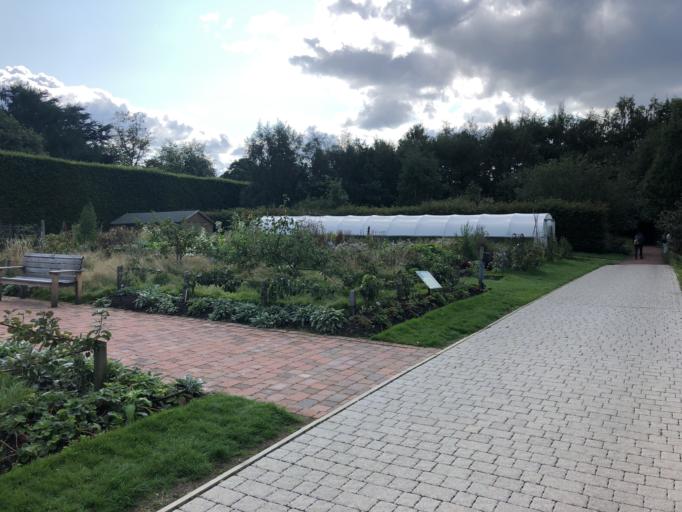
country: GB
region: Scotland
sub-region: Edinburgh
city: Edinburgh
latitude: 55.9667
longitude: -3.2120
